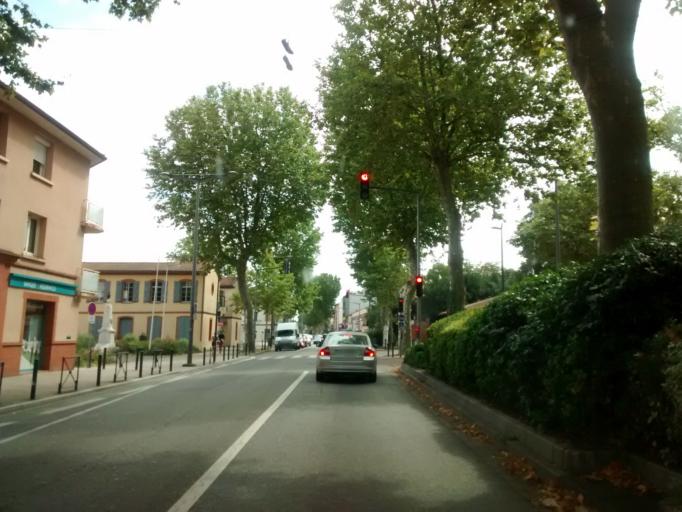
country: FR
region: Midi-Pyrenees
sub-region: Departement de la Haute-Garonne
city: L'Union
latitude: 43.6366
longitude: 1.4644
